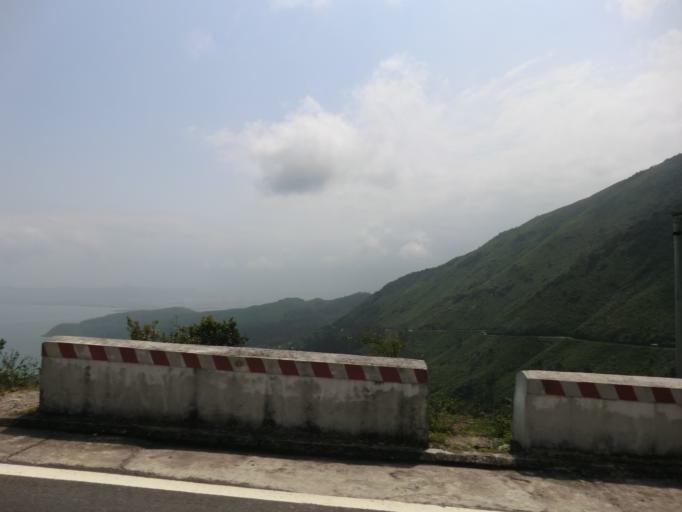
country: VN
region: Da Nang
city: Lien Chieu
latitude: 16.1849
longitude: 108.1362
